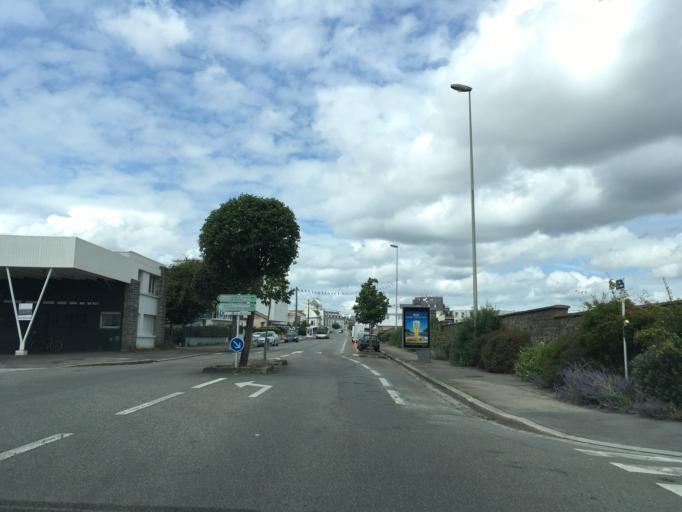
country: FR
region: Brittany
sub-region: Departement du Morbihan
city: Lorient
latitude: 47.7361
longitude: -3.3666
